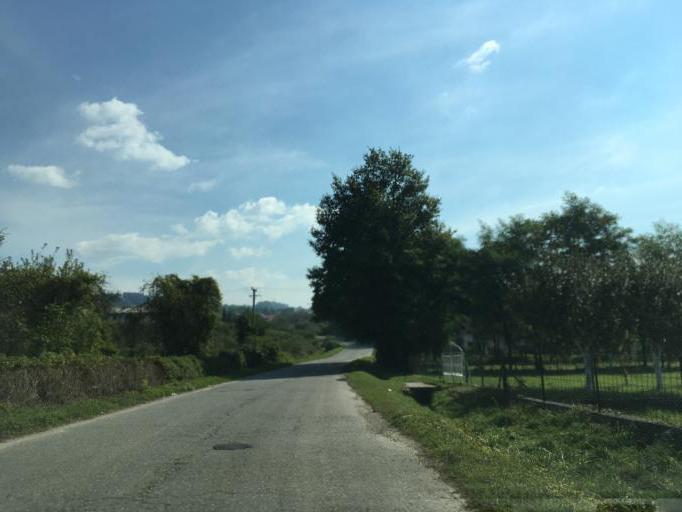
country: BA
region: Federation of Bosnia and Herzegovina
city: Bugojno
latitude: 44.0592
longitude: 17.4641
